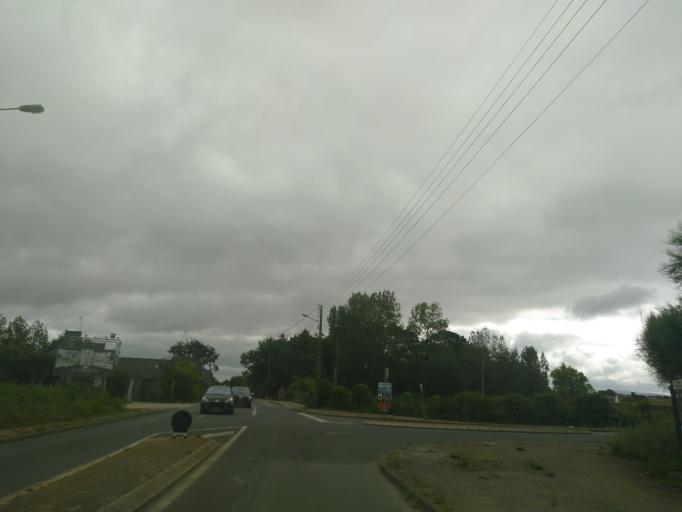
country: FR
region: Brittany
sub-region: Departement du Finistere
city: Plomodiern
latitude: 48.1693
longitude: -4.2791
